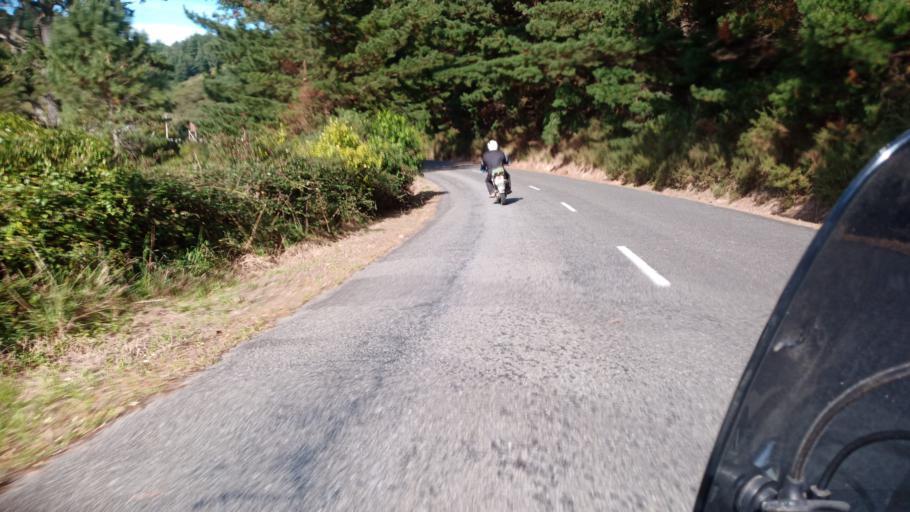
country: NZ
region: Hawke's Bay
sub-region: Wairoa District
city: Wairoa
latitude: -39.0476
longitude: 177.1188
